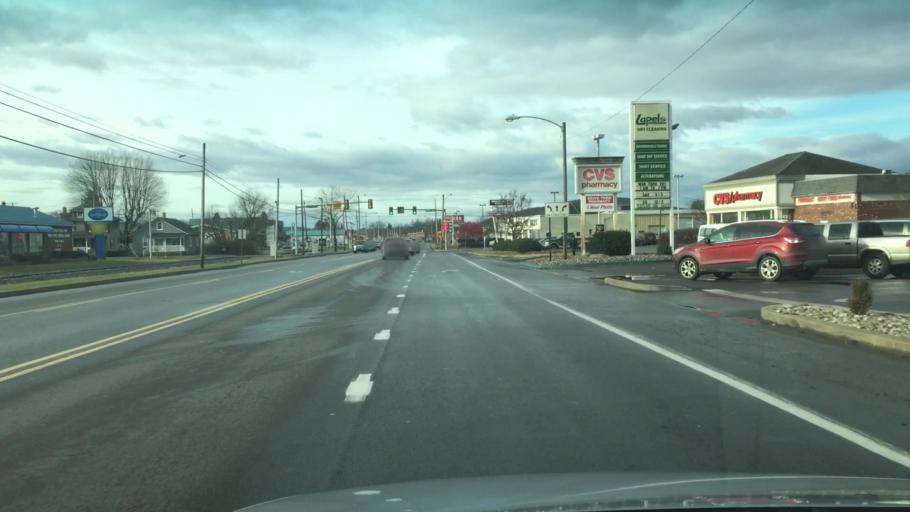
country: US
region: Pennsylvania
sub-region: Columbia County
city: Bloomsburg
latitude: 41.0037
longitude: -76.4403
